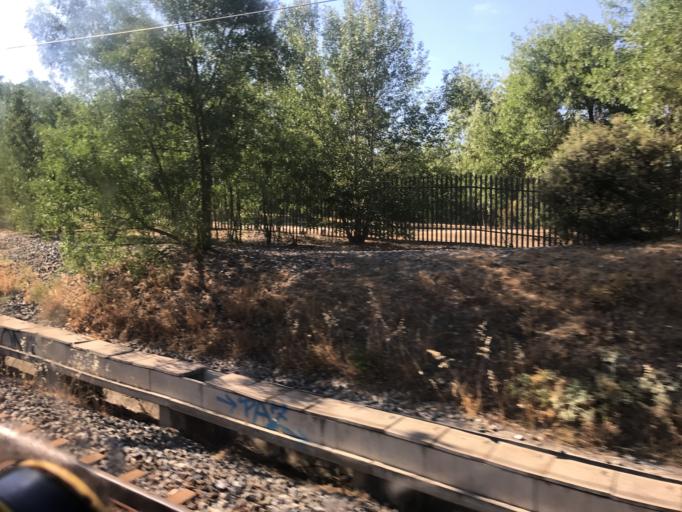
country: ES
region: Madrid
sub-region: Provincia de Madrid
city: Moncloa-Aravaca
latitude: 40.4164
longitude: -3.7395
